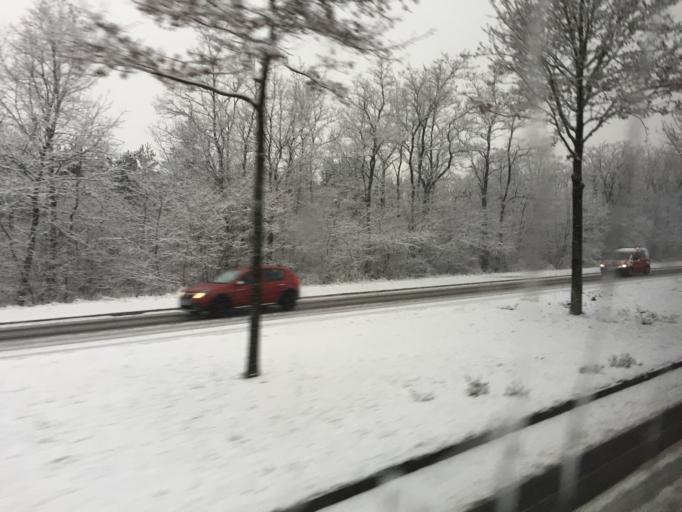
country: DE
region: Saxony
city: Albertstadt
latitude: 51.1015
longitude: 13.7357
